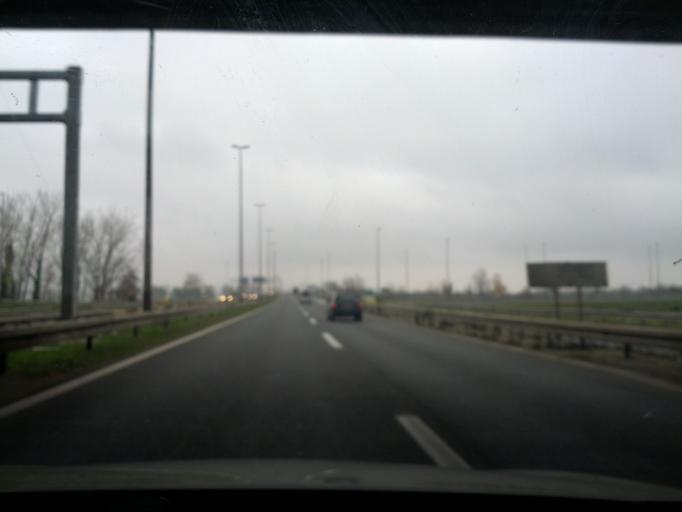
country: HR
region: Grad Zagreb
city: Jezdovec
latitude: 45.7893
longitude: 15.8490
